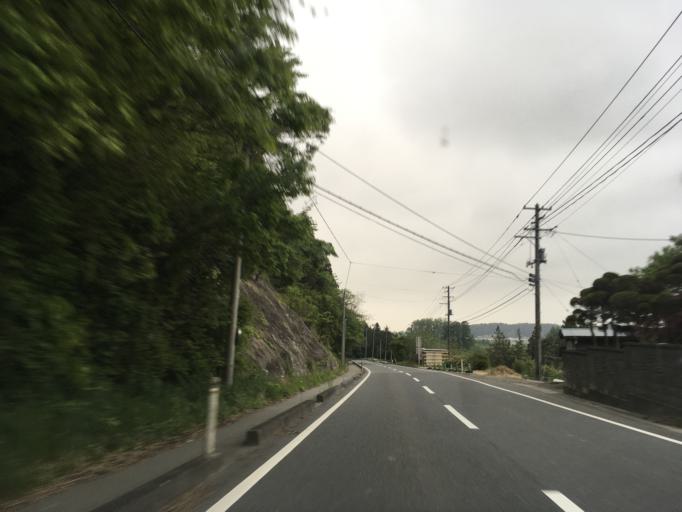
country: JP
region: Iwate
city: Ichinoseki
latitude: 38.7321
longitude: 141.3009
